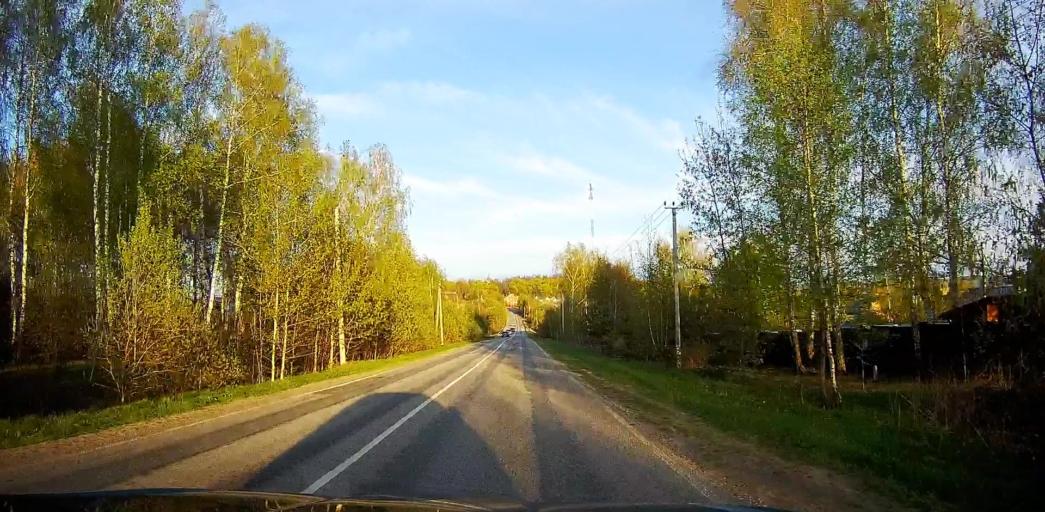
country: RU
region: Moskovskaya
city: Meshcherino
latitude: 55.2452
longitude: 38.3073
